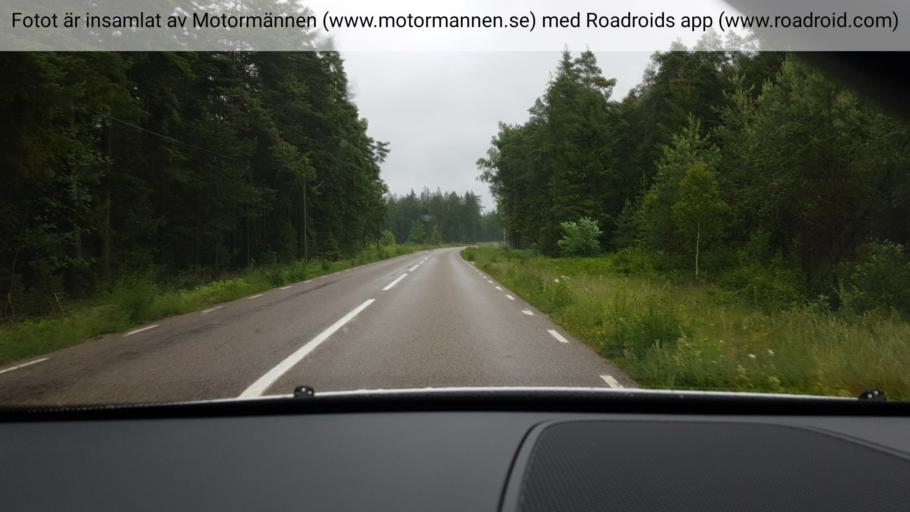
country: SE
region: Gotland
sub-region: Gotland
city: Slite
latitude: 57.6558
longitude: 18.7698
